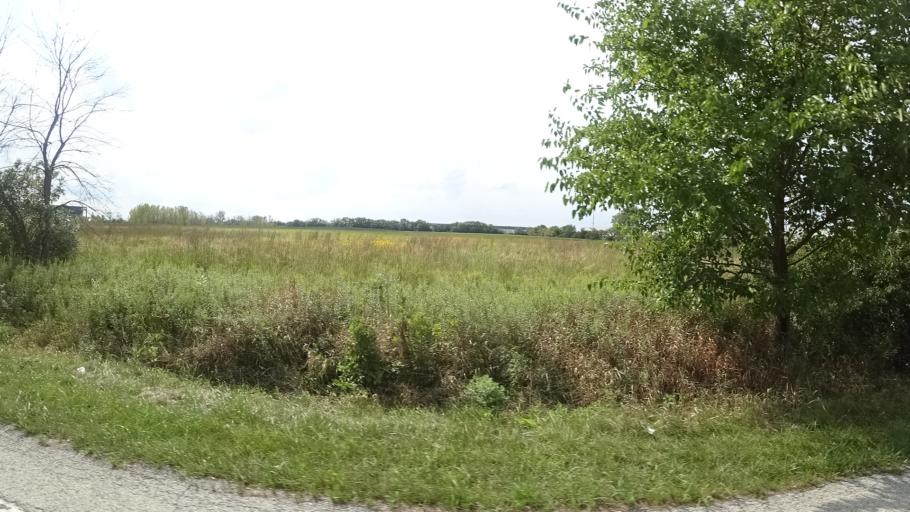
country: US
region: Illinois
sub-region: Cook County
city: Tinley Park
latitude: 41.5493
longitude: -87.7712
